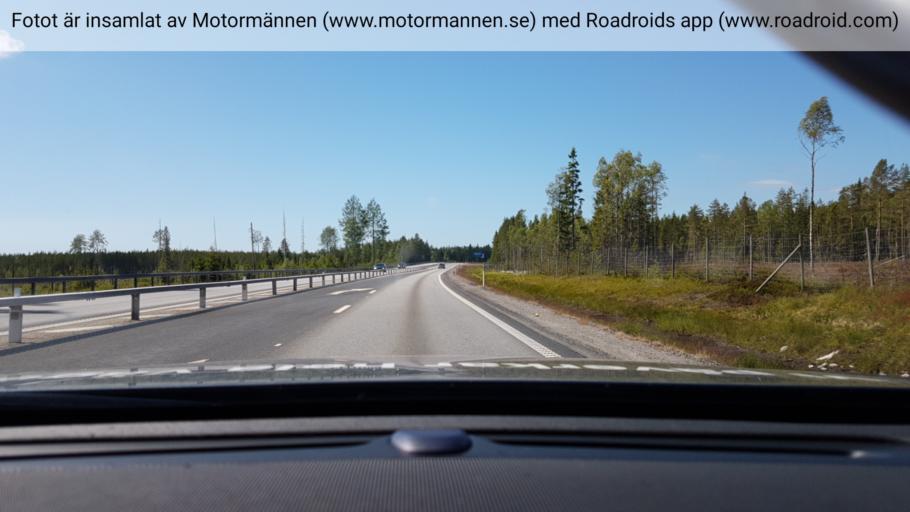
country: SE
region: Vaesterbotten
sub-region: Umea Kommun
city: Hoernefors
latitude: 63.6192
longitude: 19.8369
